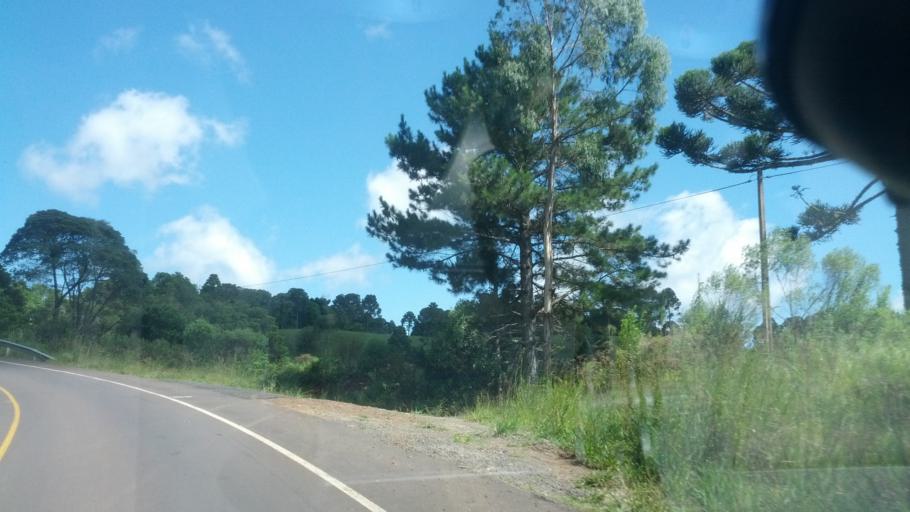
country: BR
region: Santa Catarina
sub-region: Lages
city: Lages
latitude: -27.9249
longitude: -50.5443
